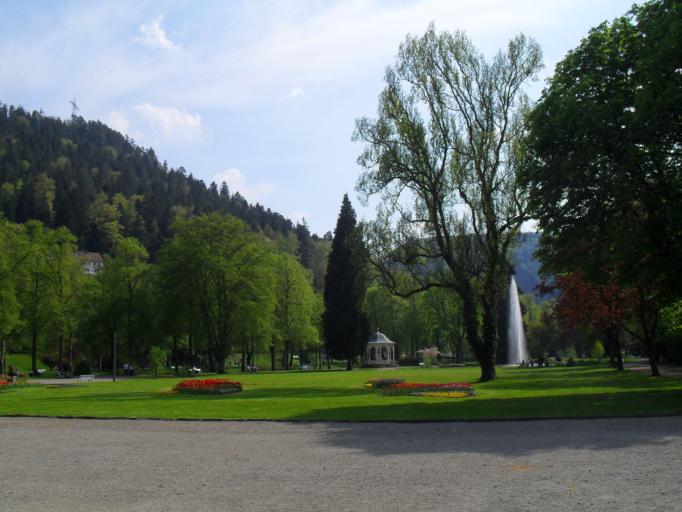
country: DE
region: Baden-Wuerttemberg
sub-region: Karlsruhe Region
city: Bad Liebenzell
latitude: 48.7706
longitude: 8.7322
